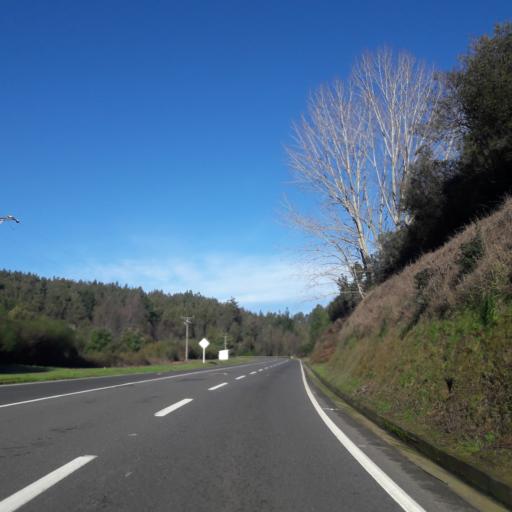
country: CL
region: Biobio
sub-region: Provincia de Biobio
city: La Laja
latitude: -37.2666
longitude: -72.9607
